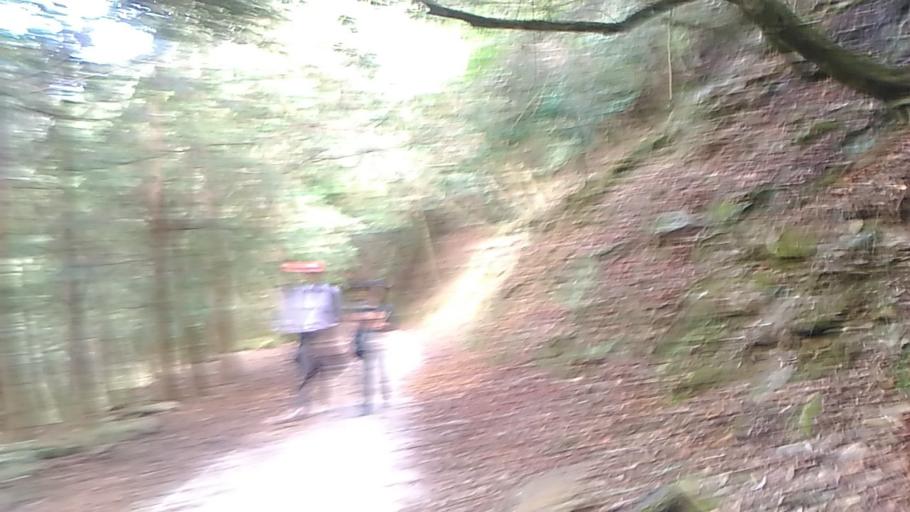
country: TW
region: Taiwan
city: Daxi
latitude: 24.4102
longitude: 121.3025
